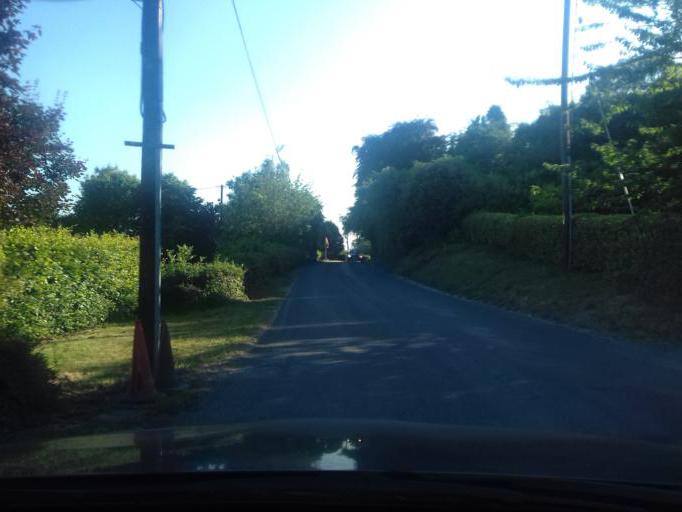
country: IE
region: Leinster
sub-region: An Mhi
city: Ashbourne
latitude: 53.4563
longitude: -6.3929
